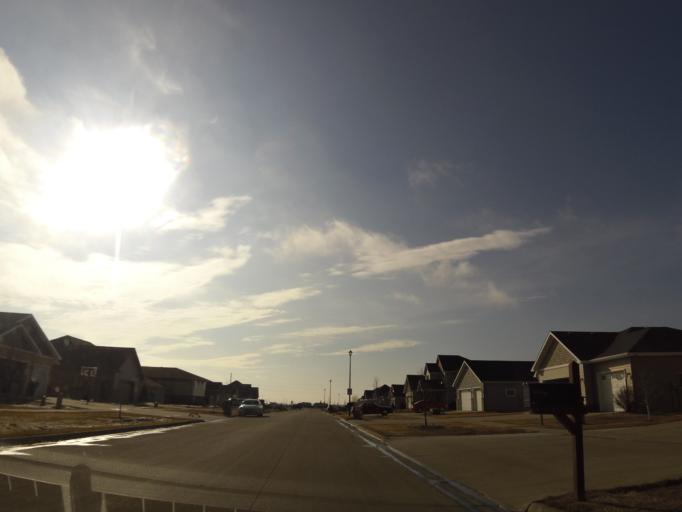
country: US
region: North Dakota
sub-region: Grand Forks County
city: Grand Forks
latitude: 47.8787
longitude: -97.0611
